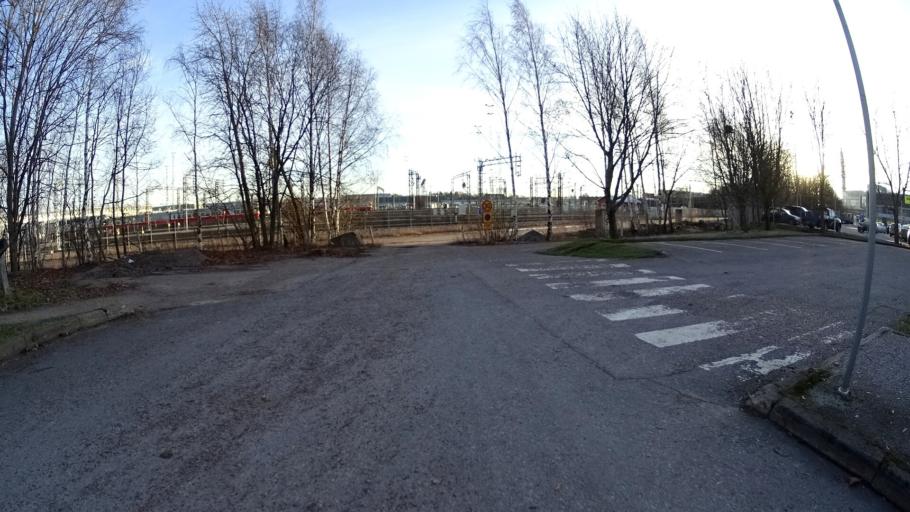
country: FI
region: Uusimaa
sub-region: Helsinki
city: Helsinki
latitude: 60.2119
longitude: 24.9201
